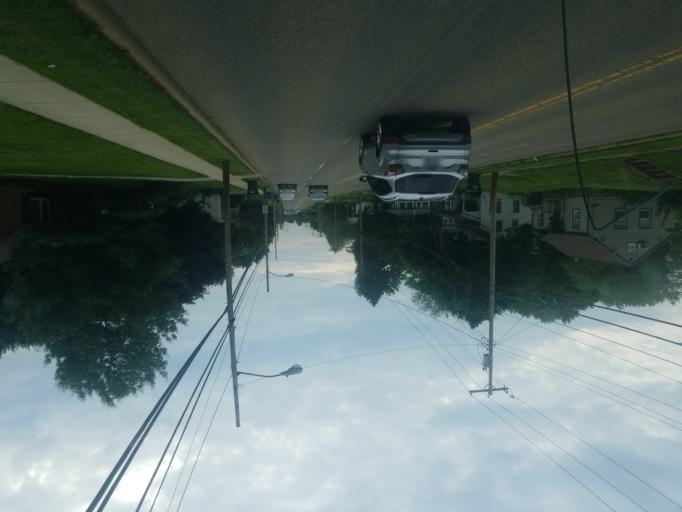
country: US
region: Ohio
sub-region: Stark County
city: Massillon
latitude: 40.7960
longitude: -81.5704
